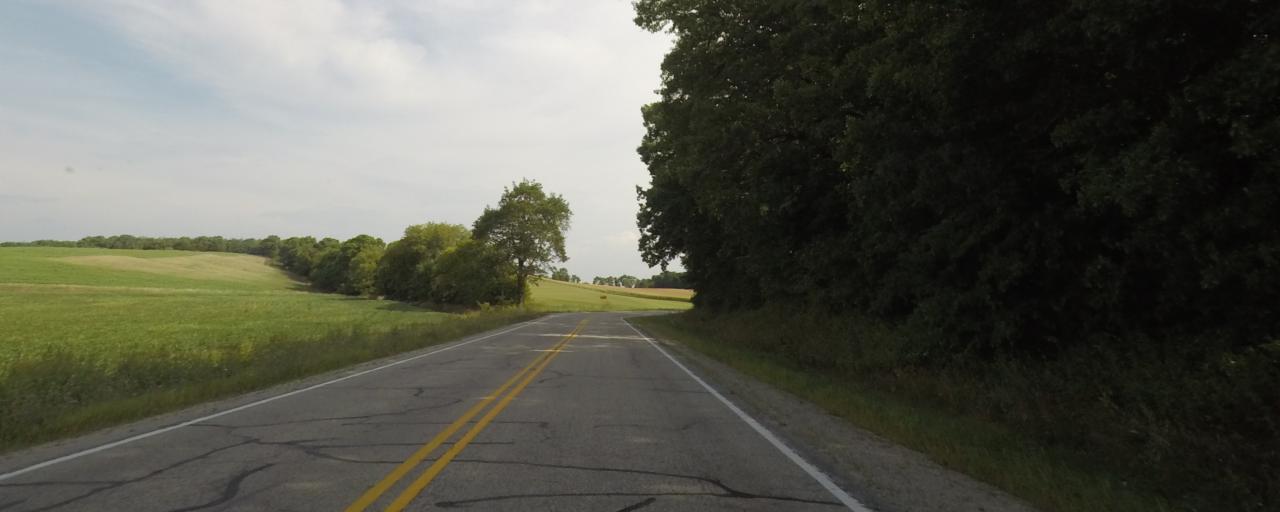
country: US
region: Wisconsin
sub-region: Jefferson County
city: Lake Koshkonong
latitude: 42.9737
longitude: -88.8997
